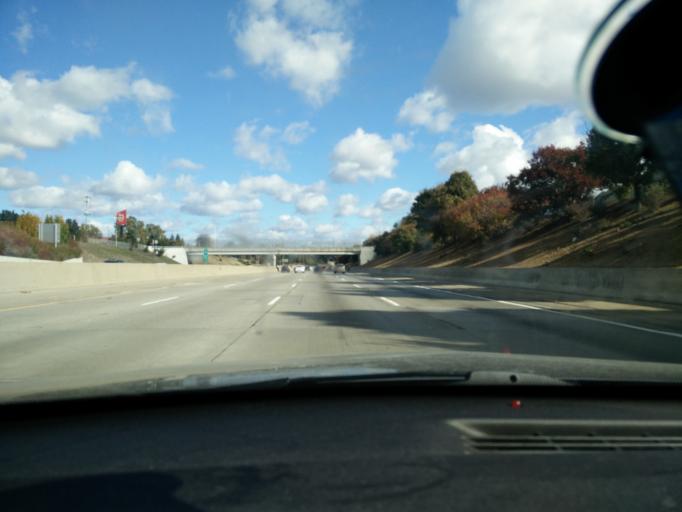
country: US
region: Michigan
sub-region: Oakland County
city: Madison Heights
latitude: 42.4842
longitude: -83.0844
